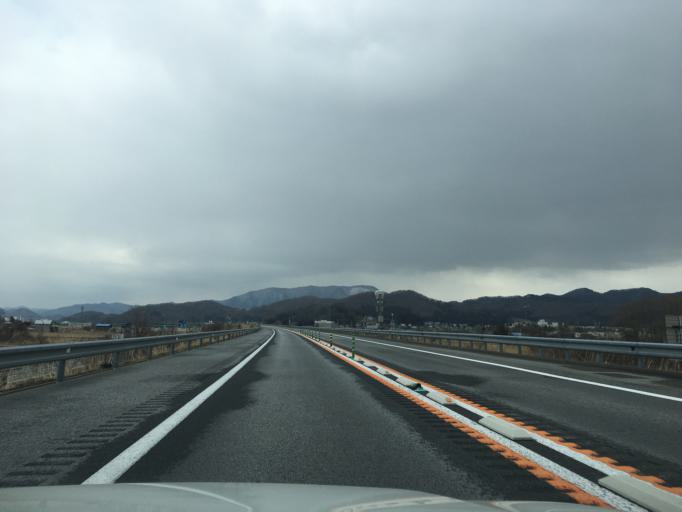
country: JP
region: Aomori
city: Aomori Shi
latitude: 40.8007
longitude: 140.7883
